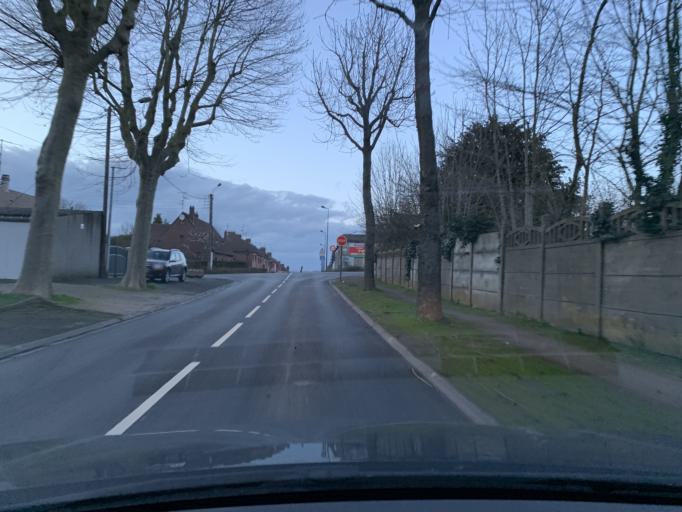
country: FR
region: Nord-Pas-de-Calais
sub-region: Departement du Nord
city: Cambrai
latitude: 50.1783
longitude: 3.2538
